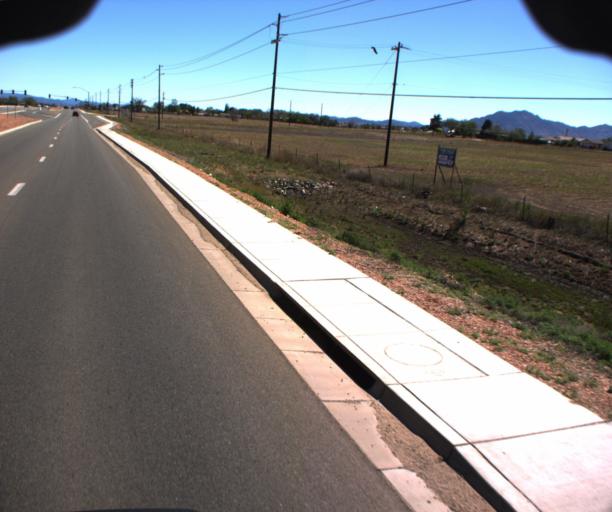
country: US
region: Arizona
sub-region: Yavapai County
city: Chino Valley
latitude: 34.7407
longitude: -112.4546
